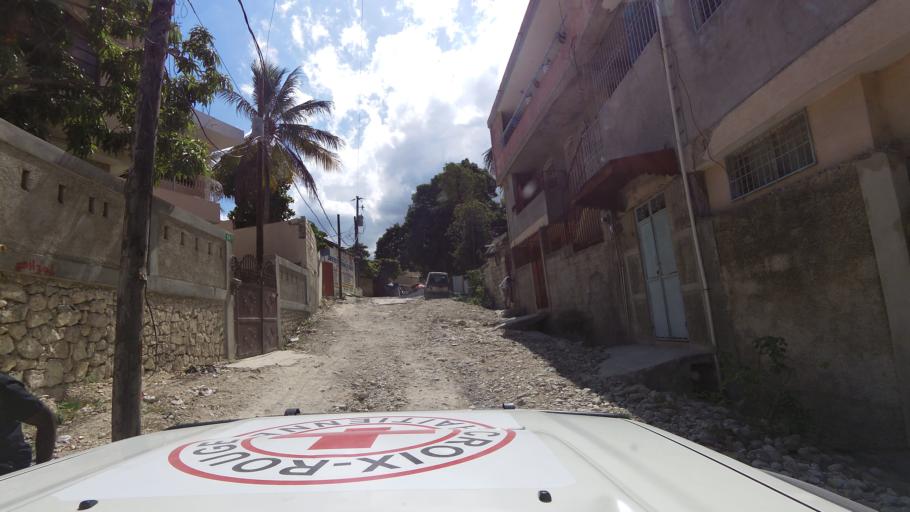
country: HT
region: Ouest
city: Delmas 73
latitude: 18.5449
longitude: -72.2988
